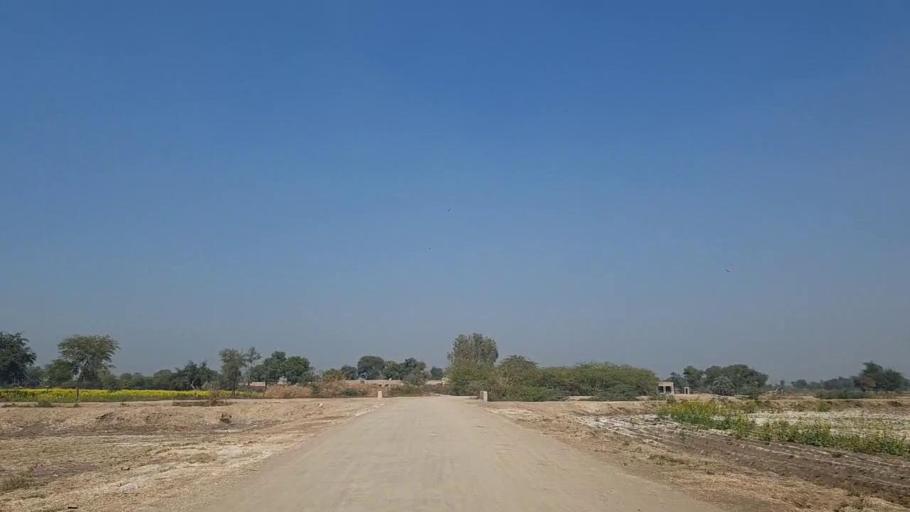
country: PK
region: Sindh
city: Nawabshah
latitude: 26.2252
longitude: 68.3431
